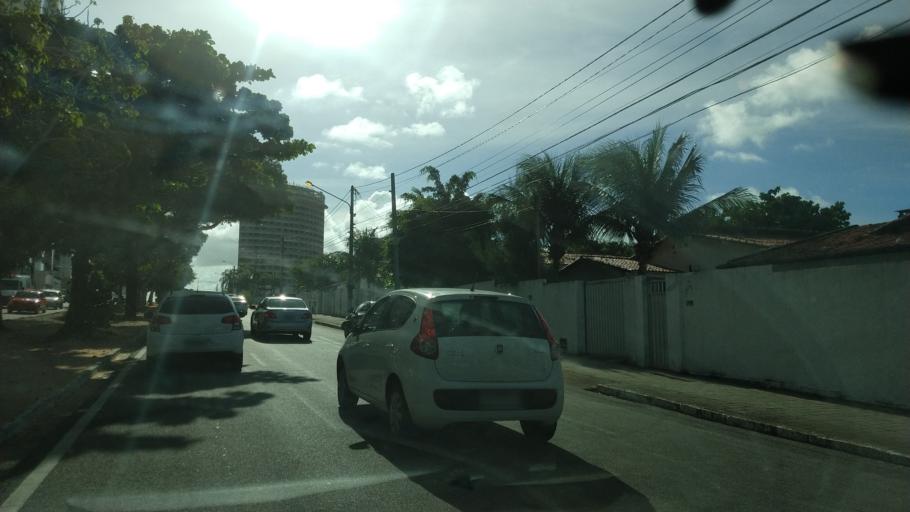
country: BR
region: Rio Grande do Norte
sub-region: Natal
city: Natal
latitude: -5.8082
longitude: -35.2010
